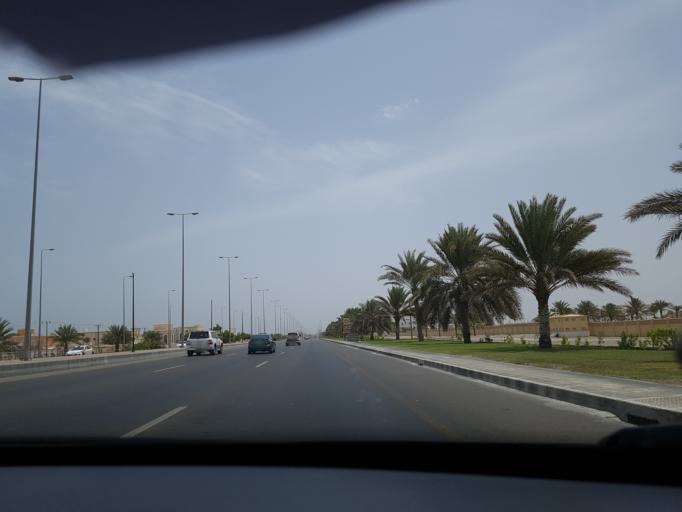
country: OM
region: Muhafazat Masqat
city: As Sib al Jadidah
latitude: 23.6790
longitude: 58.1202
